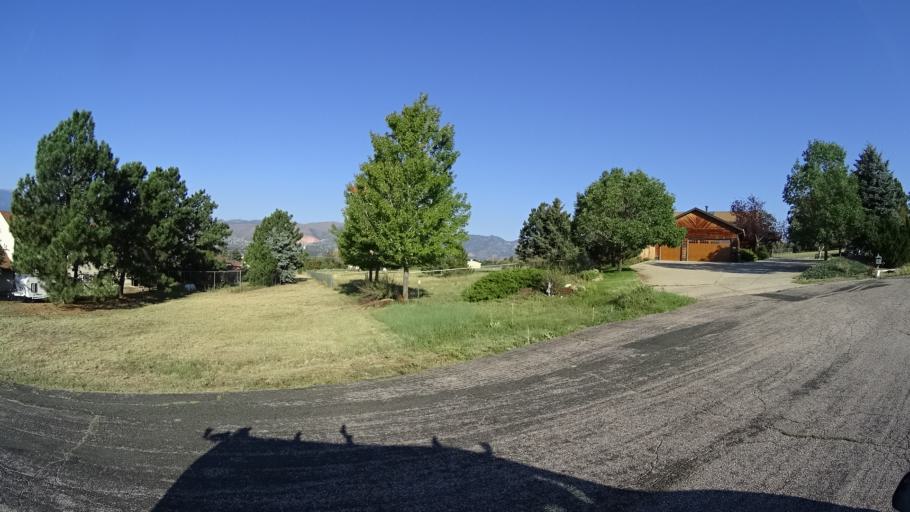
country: US
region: Colorado
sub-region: El Paso County
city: Air Force Academy
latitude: 38.9341
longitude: -104.7793
